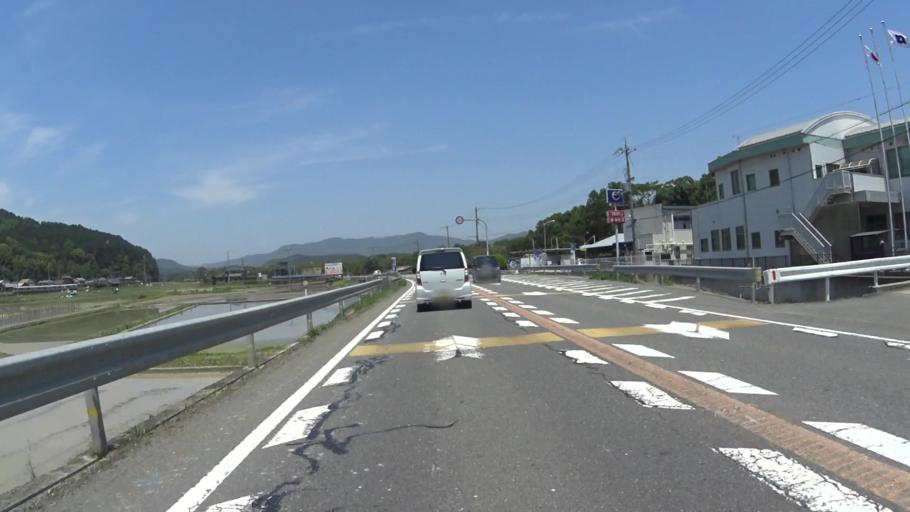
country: JP
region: Kyoto
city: Kameoka
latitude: 35.0558
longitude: 135.5479
